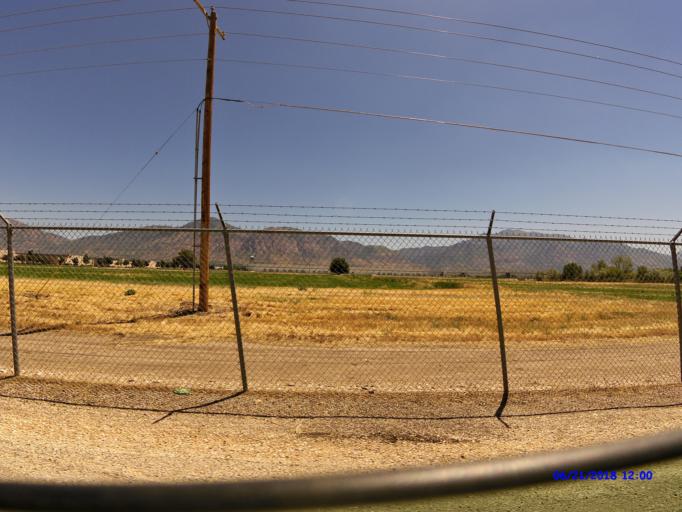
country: US
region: Utah
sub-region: Weber County
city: Marriott-Slaterville
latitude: 41.2565
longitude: -112.0089
